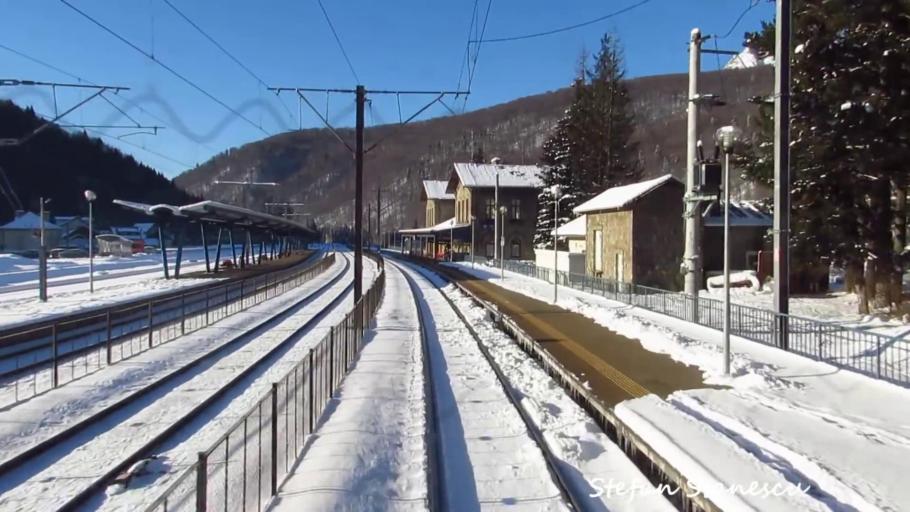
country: RO
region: Prahova
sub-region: Oras Azuga
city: Azuga
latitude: 45.4444
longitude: 25.5522
